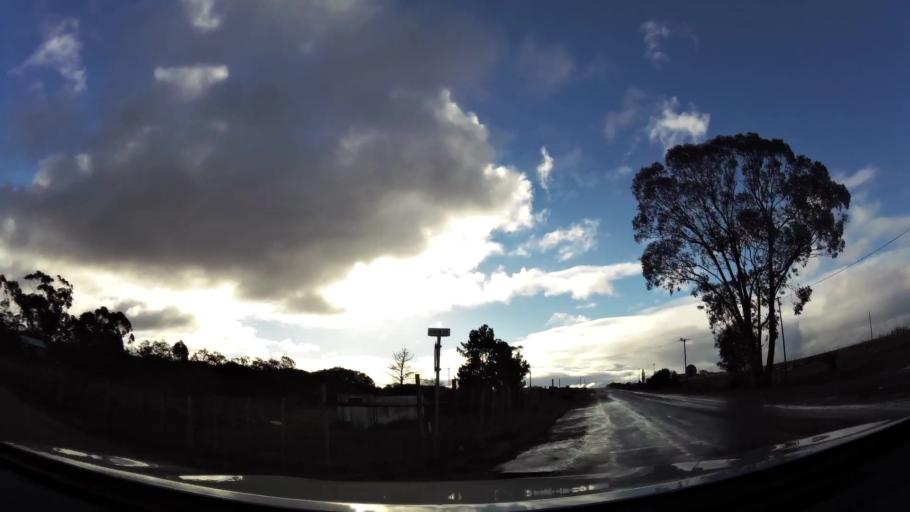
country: ZA
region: Western Cape
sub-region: Eden District Municipality
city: Riversdale
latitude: -34.1983
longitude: 21.5831
